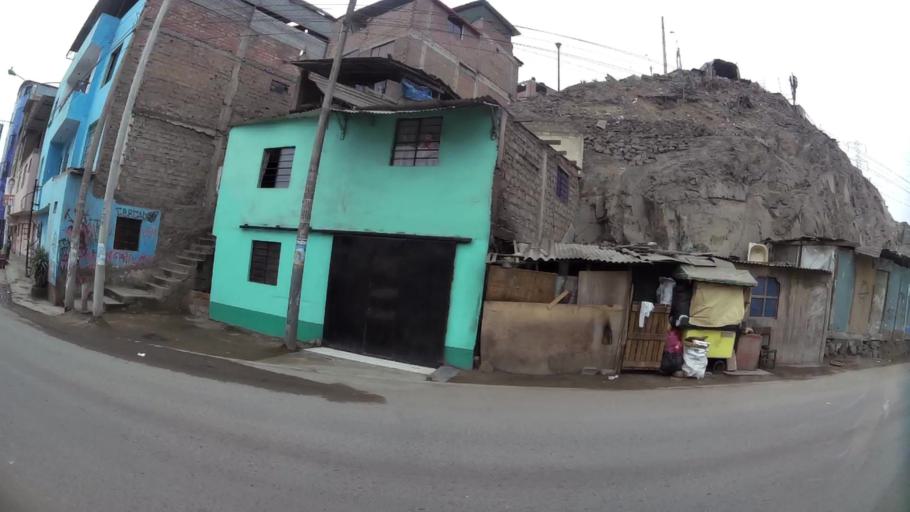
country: PE
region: Lima
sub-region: Lima
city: Surco
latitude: -12.1760
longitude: -76.9406
